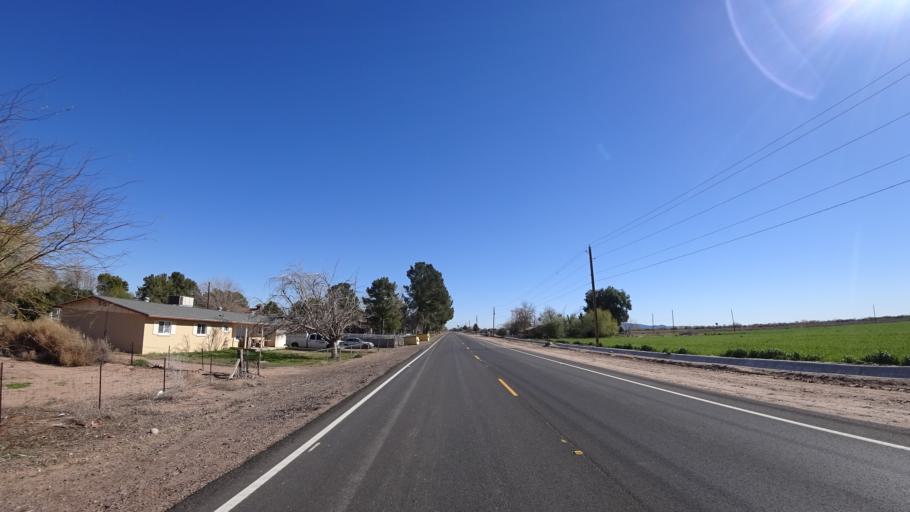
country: US
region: Arizona
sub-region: Maricopa County
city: Tolleson
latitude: 33.3919
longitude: -112.2948
